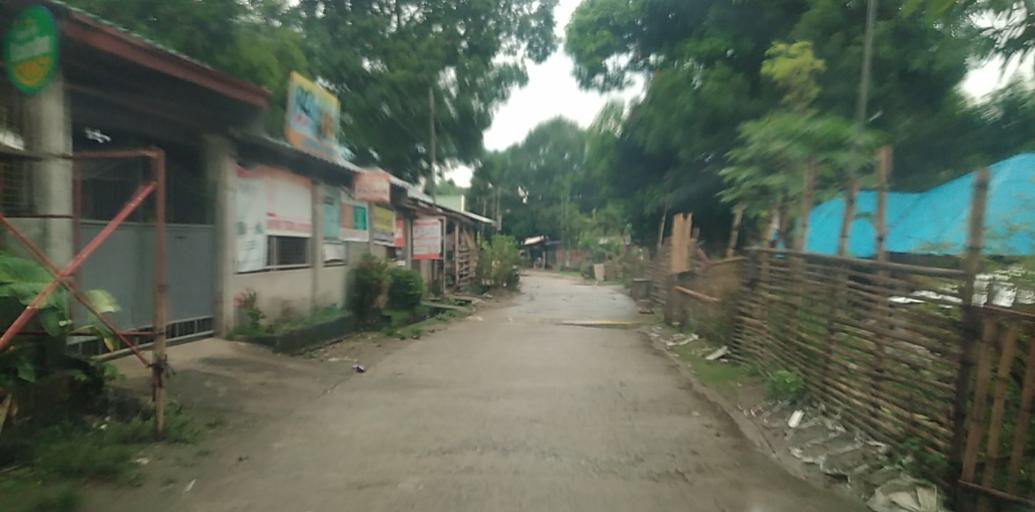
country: PH
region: Central Luzon
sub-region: Province of Pampanga
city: Arayat
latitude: 15.1533
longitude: 120.7427
